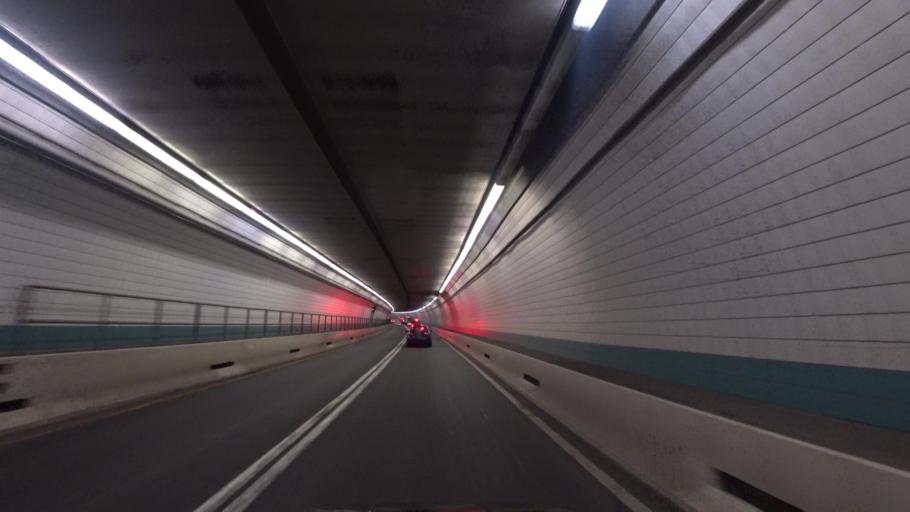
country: US
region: Massachusetts
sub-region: Suffolk County
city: South Boston
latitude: 42.3476
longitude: -71.0328
